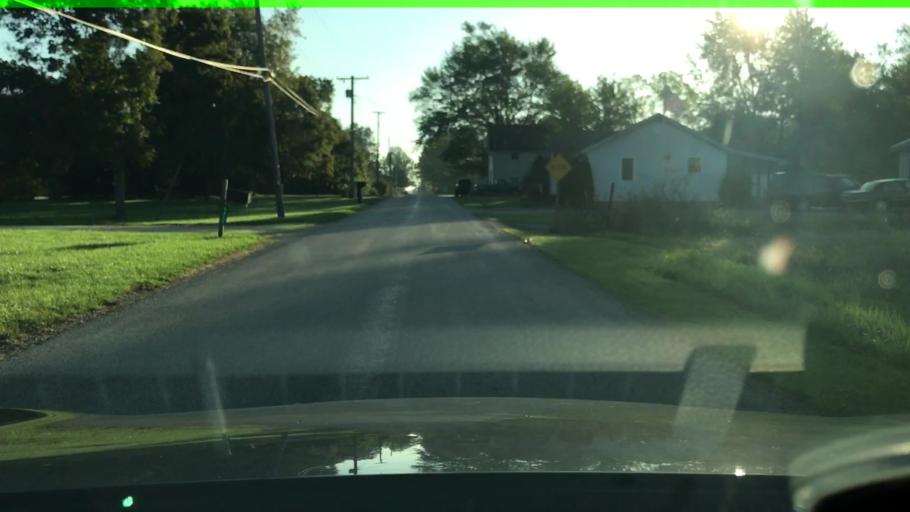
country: US
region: Indiana
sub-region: Jay County
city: Dunkirk
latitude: 40.4062
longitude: -85.2792
